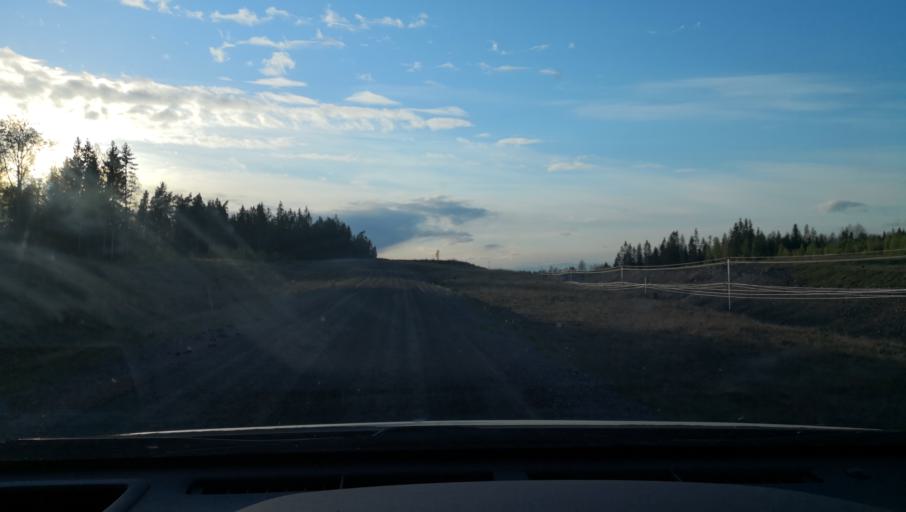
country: SE
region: OErebro
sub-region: Askersunds Kommun
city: Asbro
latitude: 58.8804
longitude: 15.1394
